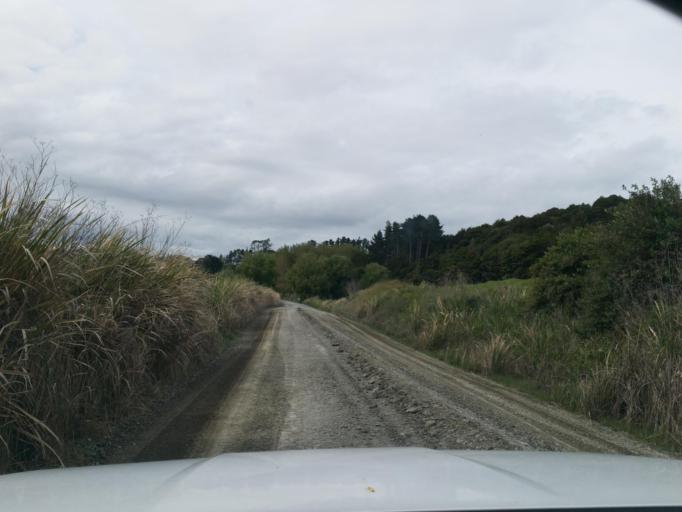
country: NZ
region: Northland
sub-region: Kaipara District
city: Dargaville
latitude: -35.9130
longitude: 173.9208
